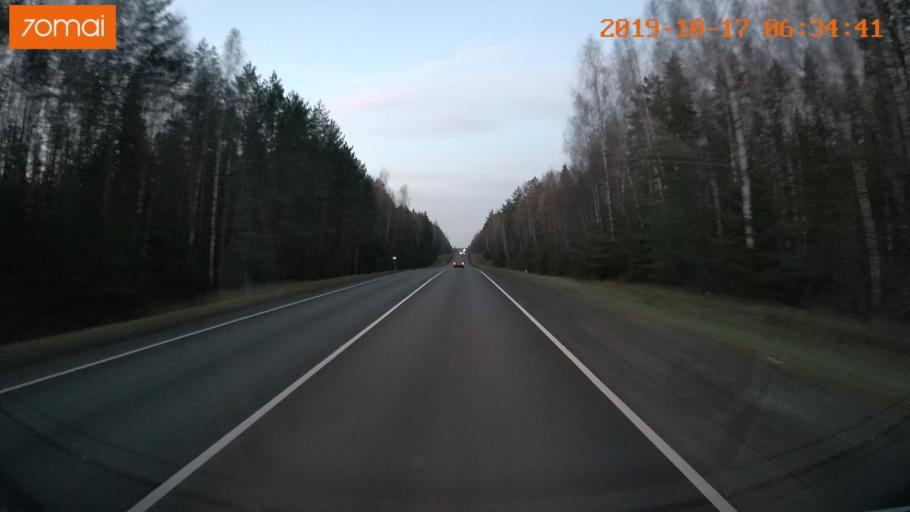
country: RU
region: Ivanovo
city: Novoye Leushino
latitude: 56.7006
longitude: 40.6343
